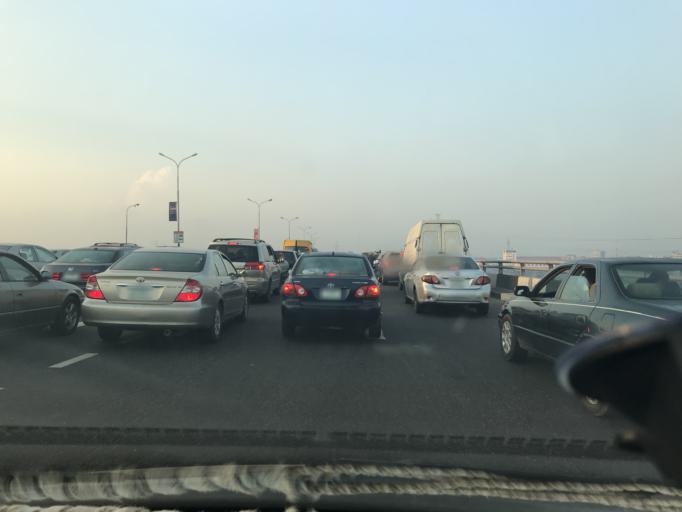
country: NG
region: Lagos
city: Ebute Metta
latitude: 6.4833
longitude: 3.3931
